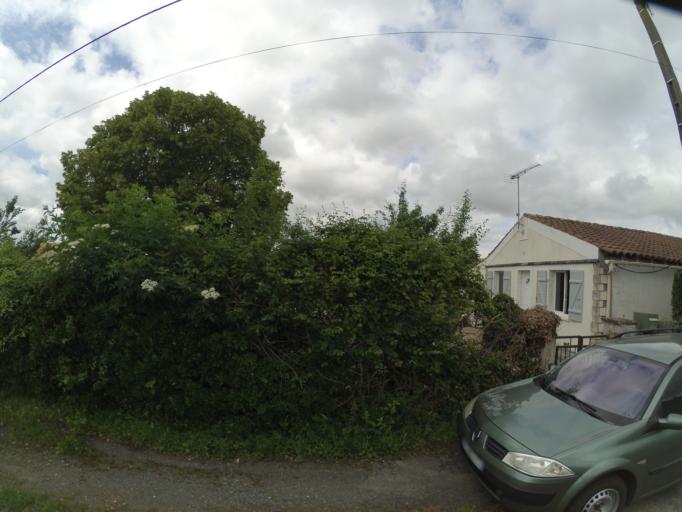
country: FR
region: Poitou-Charentes
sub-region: Departement de la Charente-Maritime
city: Breuil-Magne
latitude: 45.9631
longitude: -0.9700
